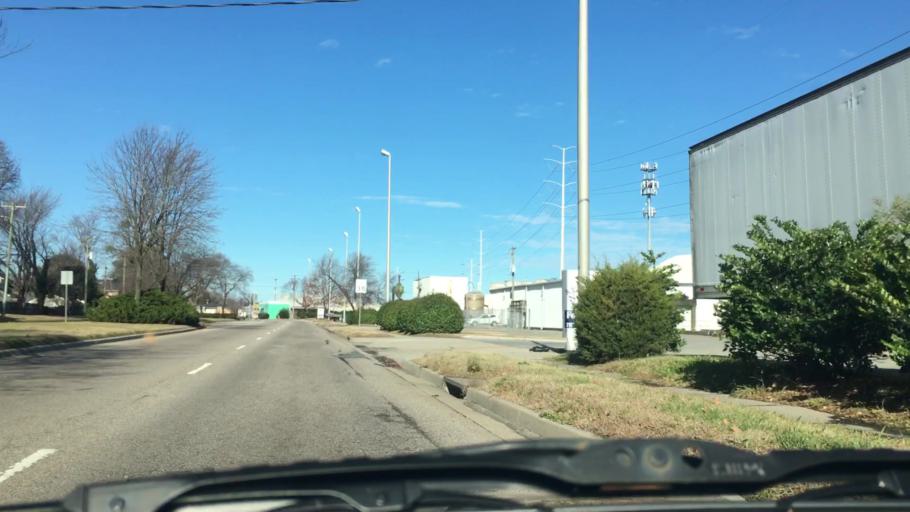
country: US
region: Virginia
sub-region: City of Norfolk
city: Norfolk
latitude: 36.8720
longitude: -76.2509
